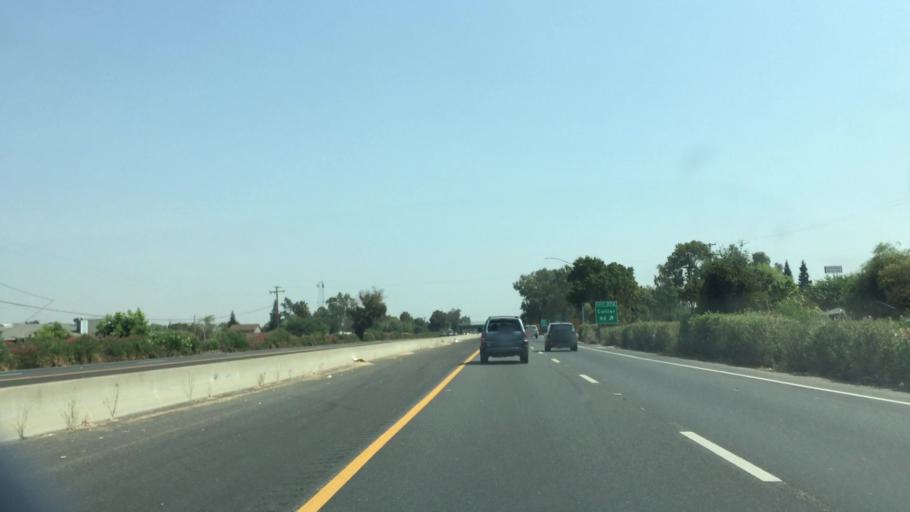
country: US
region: California
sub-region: San Joaquin County
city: Collierville
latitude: 38.2230
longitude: -121.2737
